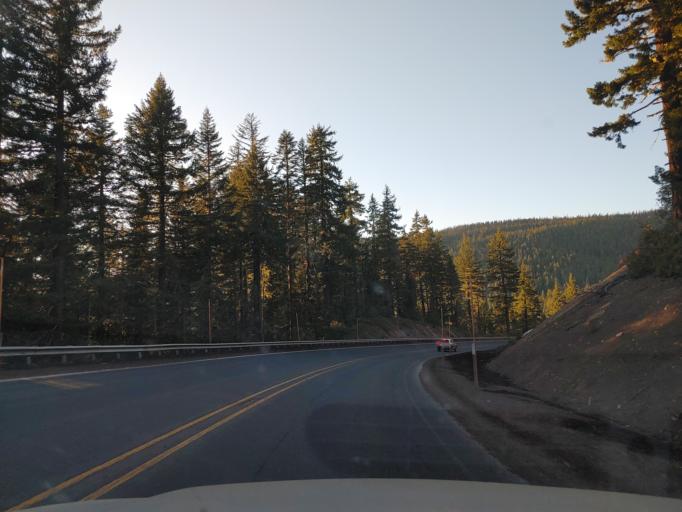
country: US
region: Oregon
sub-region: Lane County
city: Oakridge
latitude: 43.6144
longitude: -122.0693
